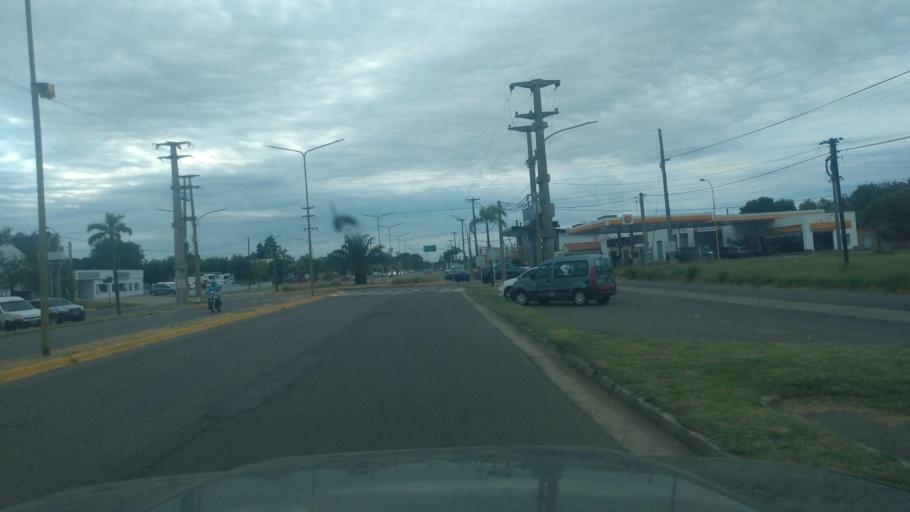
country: AR
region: Buenos Aires
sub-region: Partido de Trenque Lauquen
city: Trenque Lauquen
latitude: -35.9820
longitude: -62.7269
